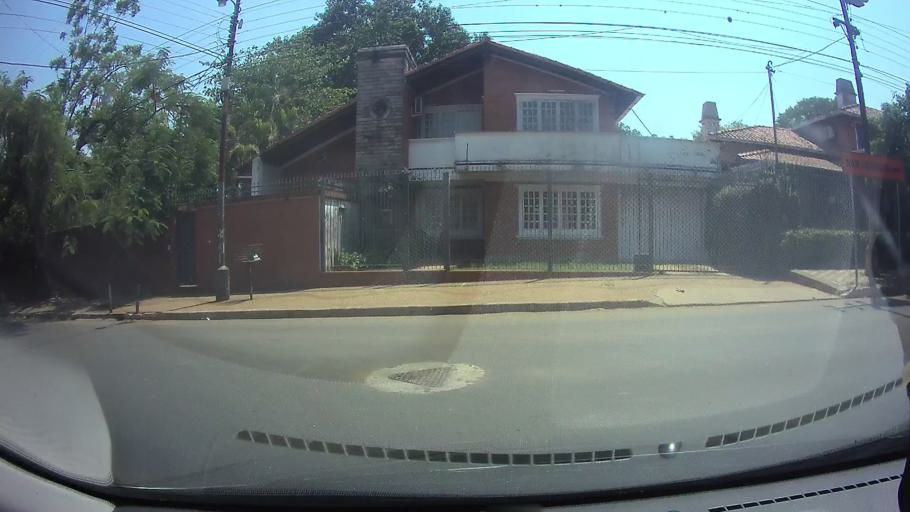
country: PY
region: Central
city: Fernando de la Mora
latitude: -25.3252
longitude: -57.5425
